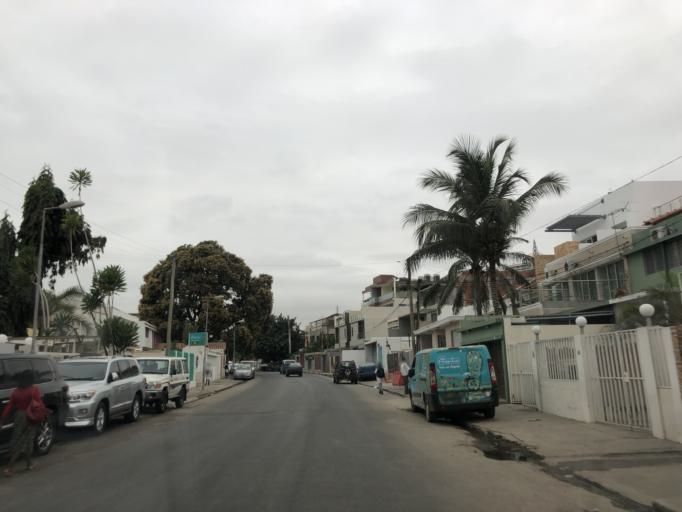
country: AO
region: Luanda
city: Luanda
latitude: -8.8321
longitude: 13.2321
